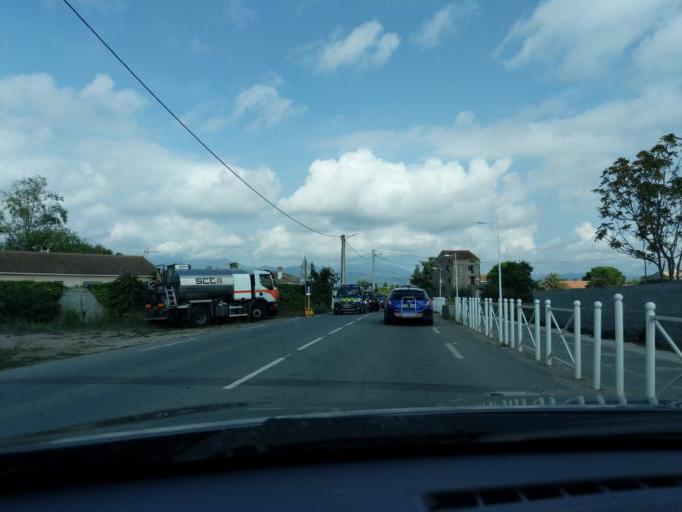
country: FR
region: Corsica
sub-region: Departement de la Haute-Corse
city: Ghisonaccia
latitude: 42.0102
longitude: 9.4115
